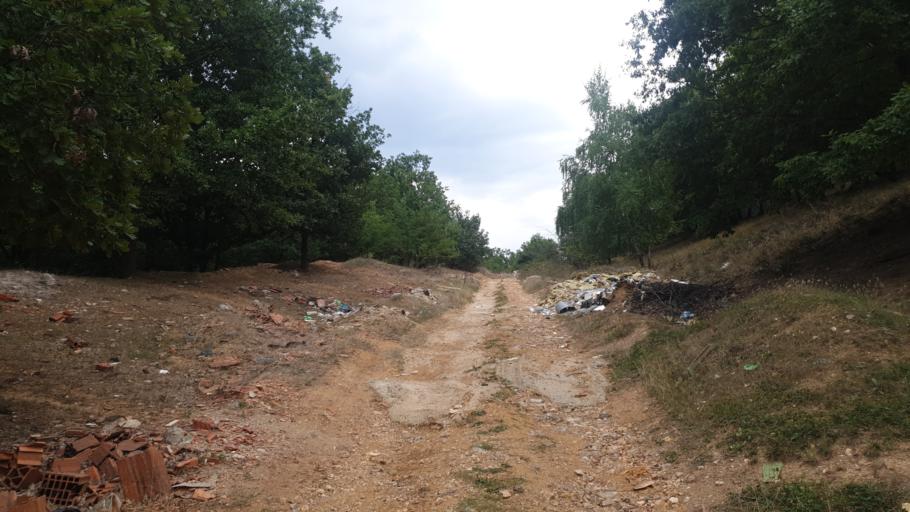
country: MK
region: Kicevo
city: Zajas
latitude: 41.5725
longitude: 20.9458
